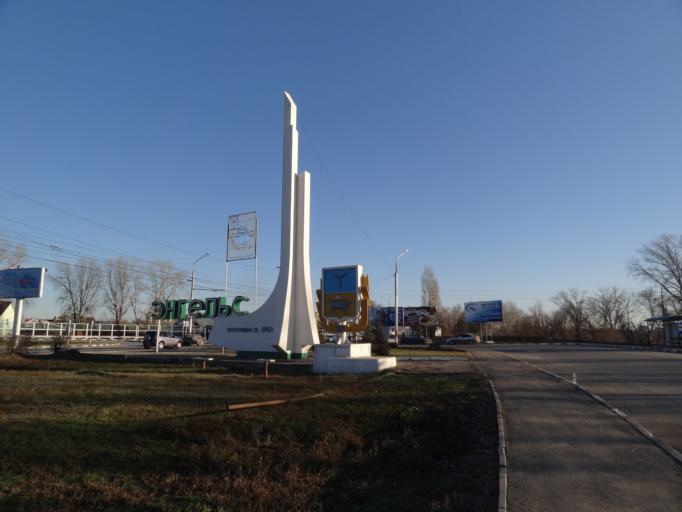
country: RU
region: Saratov
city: Engel's
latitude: 51.5031
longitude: 46.0794
